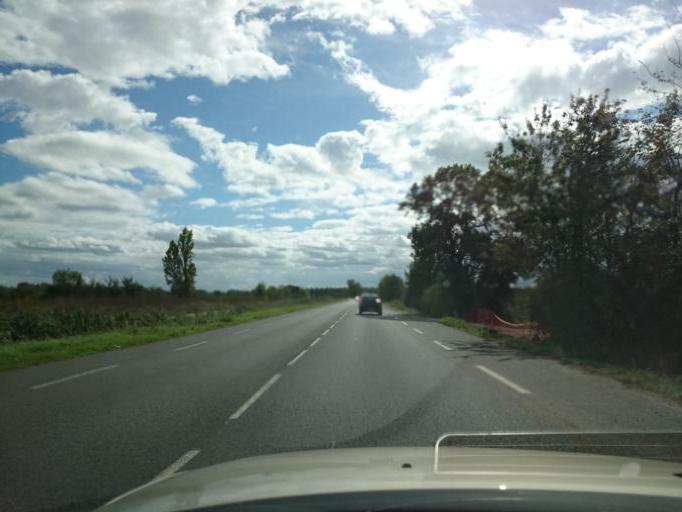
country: FR
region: Aquitaine
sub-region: Departement de la Gironde
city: Saint-Louis-de-Montferrand
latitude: 44.9416
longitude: -0.5610
